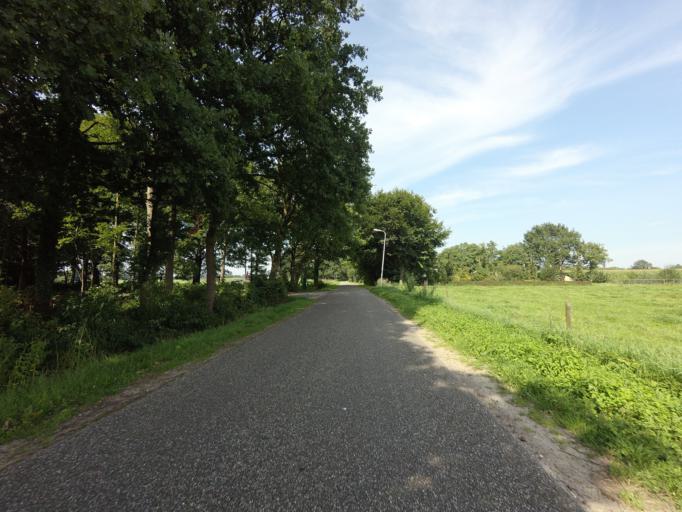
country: NL
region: Overijssel
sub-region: Gemeente Borne
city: Borne
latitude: 52.3121
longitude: 6.7149
